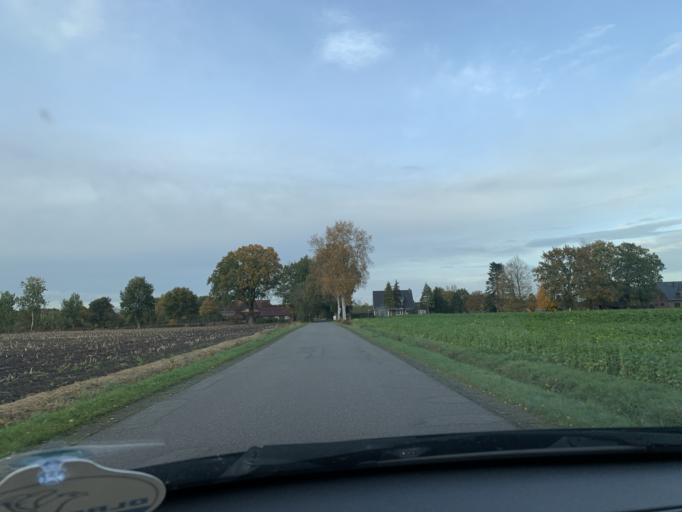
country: DE
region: Lower Saxony
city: Bad Zwischenahn
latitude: 53.2273
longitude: 8.0452
